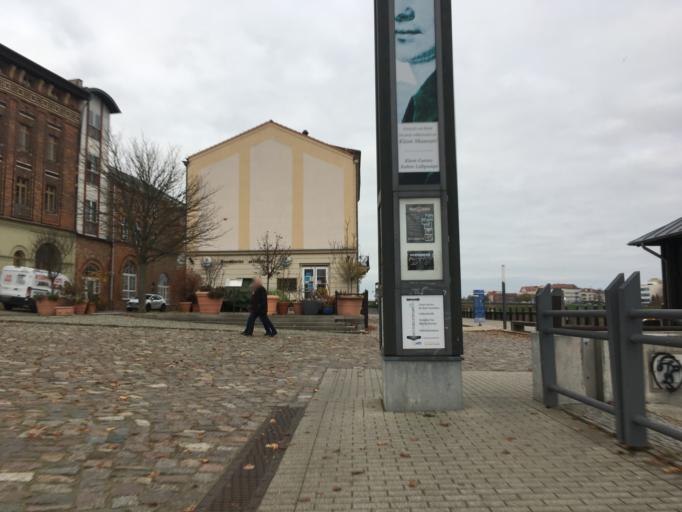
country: PL
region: Lubusz
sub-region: Powiat slubicki
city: Slubice
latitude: 52.3441
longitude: 14.5579
